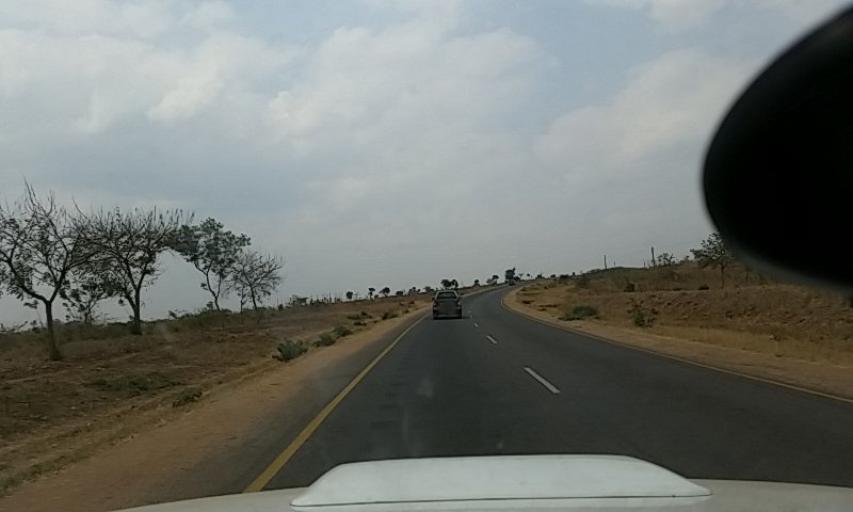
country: MW
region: Central Region
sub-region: Lilongwe District
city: Lilongwe
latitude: -13.8451
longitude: 33.8406
